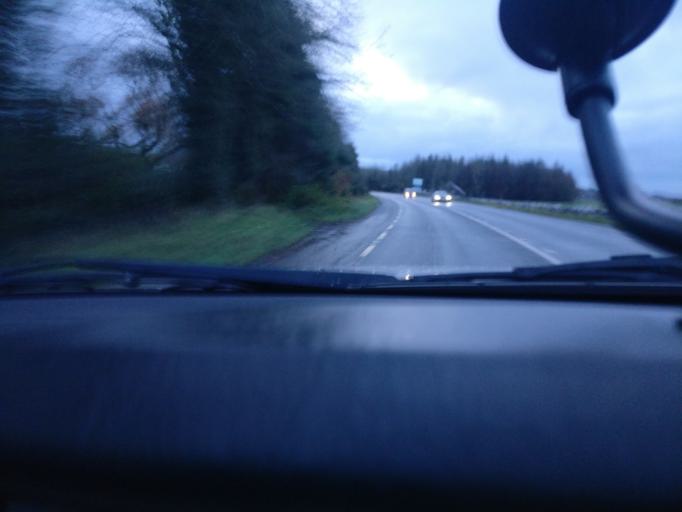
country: IE
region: Connaught
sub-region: County Galway
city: Loughrea
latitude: 53.2204
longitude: -8.4775
